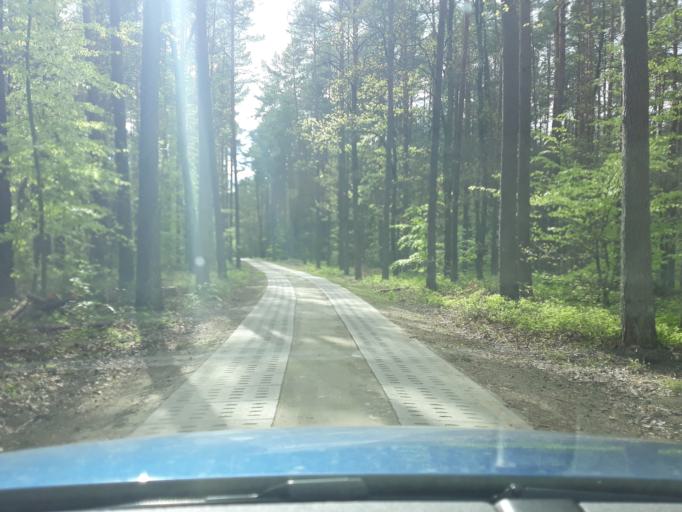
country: PL
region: Pomeranian Voivodeship
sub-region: Powiat czluchowski
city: Czluchow
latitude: 53.7428
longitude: 17.3492
